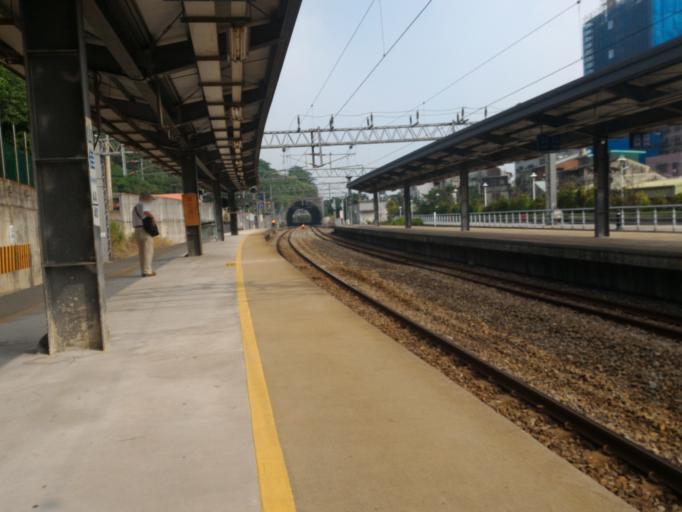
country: TW
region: Taiwan
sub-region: Taoyuan
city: Taoyuan
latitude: 24.9728
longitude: 121.3931
